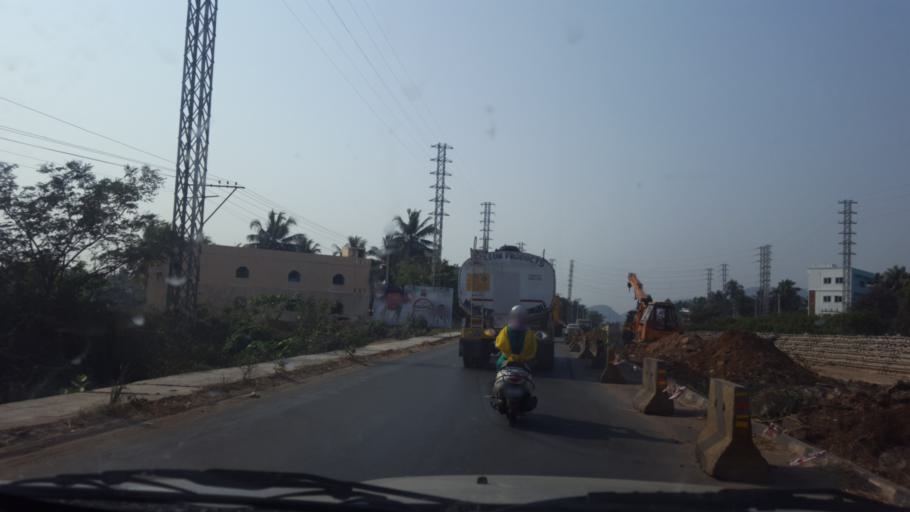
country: IN
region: Andhra Pradesh
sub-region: Vishakhapatnam
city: Anakapalle
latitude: 17.6750
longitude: 82.9974
